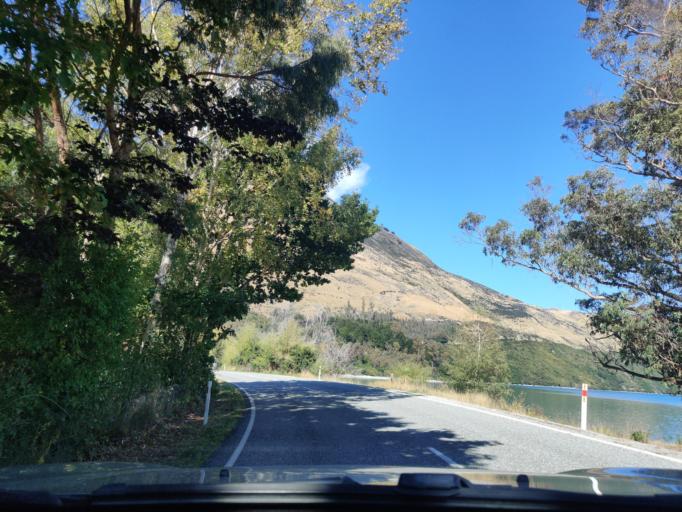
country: NZ
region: Otago
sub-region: Queenstown-Lakes District
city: Queenstown
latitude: -45.0010
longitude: 168.4390
